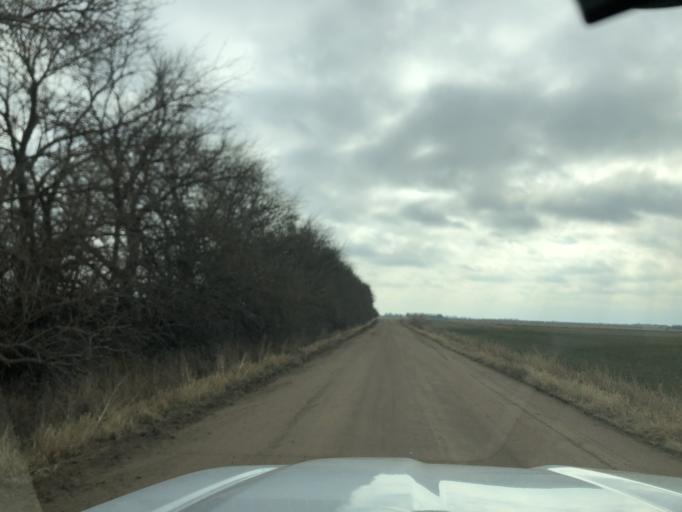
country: US
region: Kansas
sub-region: Reno County
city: Nickerson
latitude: 37.9881
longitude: -98.2157
